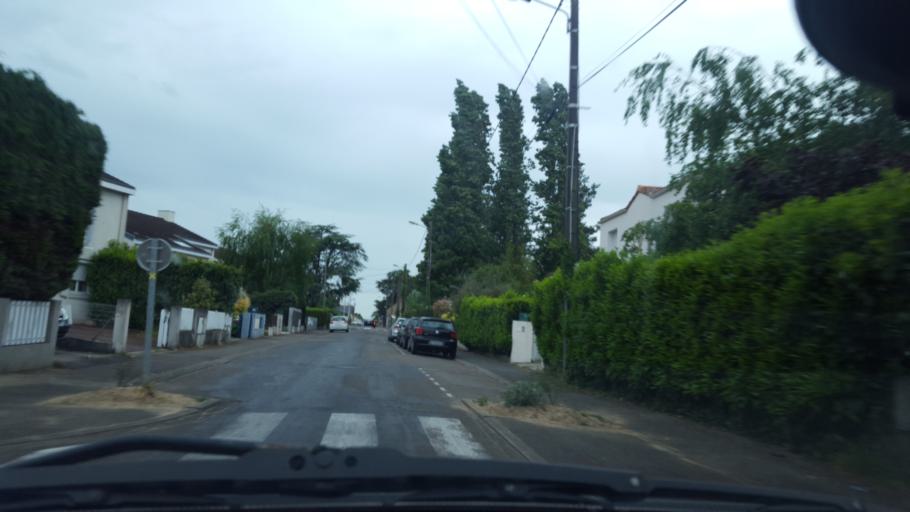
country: FR
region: Pays de la Loire
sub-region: Departement de la Loire-Atlantique
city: Reze
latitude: 47.1746
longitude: -1.5387
